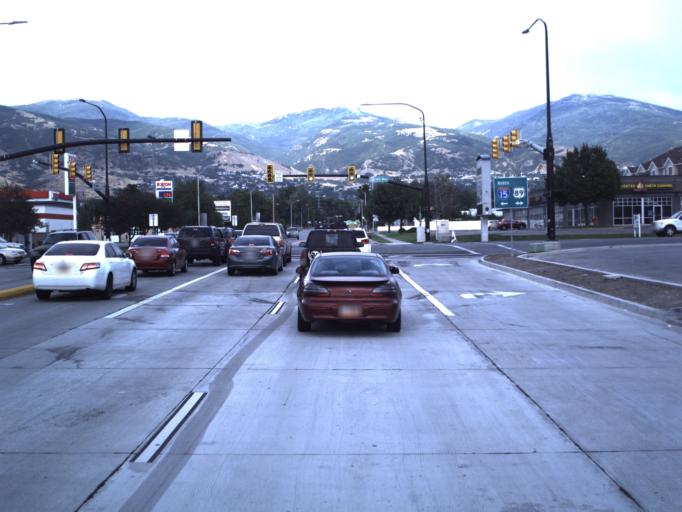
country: US
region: Utah
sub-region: Davis County
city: West Bountiful
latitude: 40.8940
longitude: -111.8930
